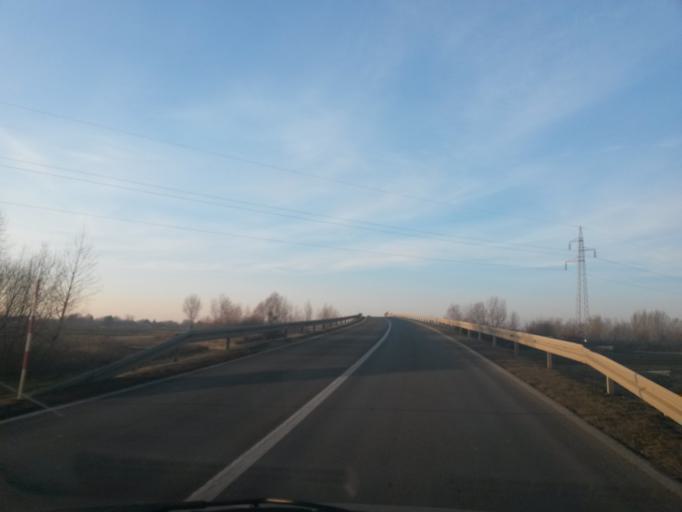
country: HR
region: Varazdinska
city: Jalzabet
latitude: 46.2935
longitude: 16.4961
